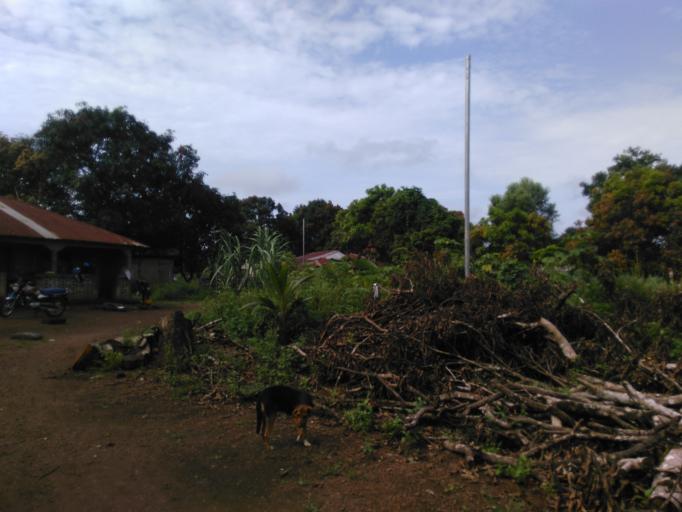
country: SL
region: Southern Province
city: Rotifunk
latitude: 8.4851
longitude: -12.7566
